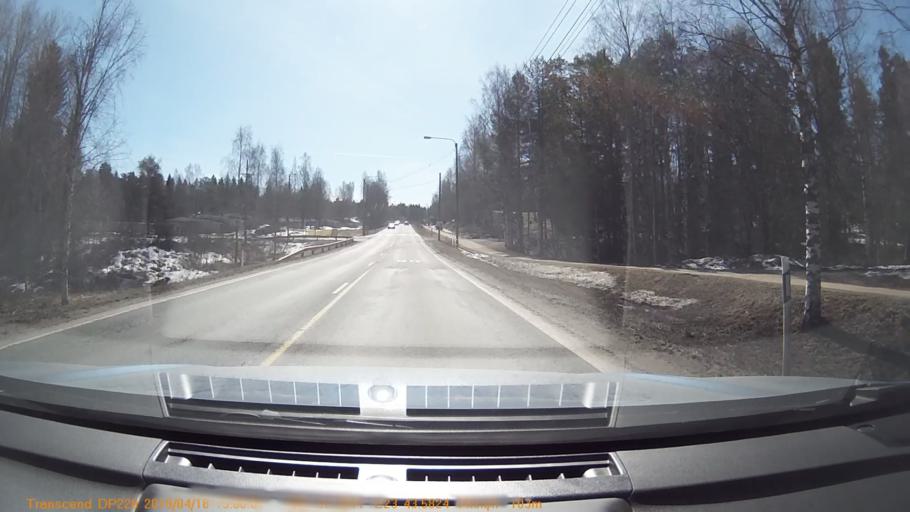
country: FI
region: Pirkanmaa
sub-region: Tampere
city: Kuru
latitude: 61.8730
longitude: 23.7268
